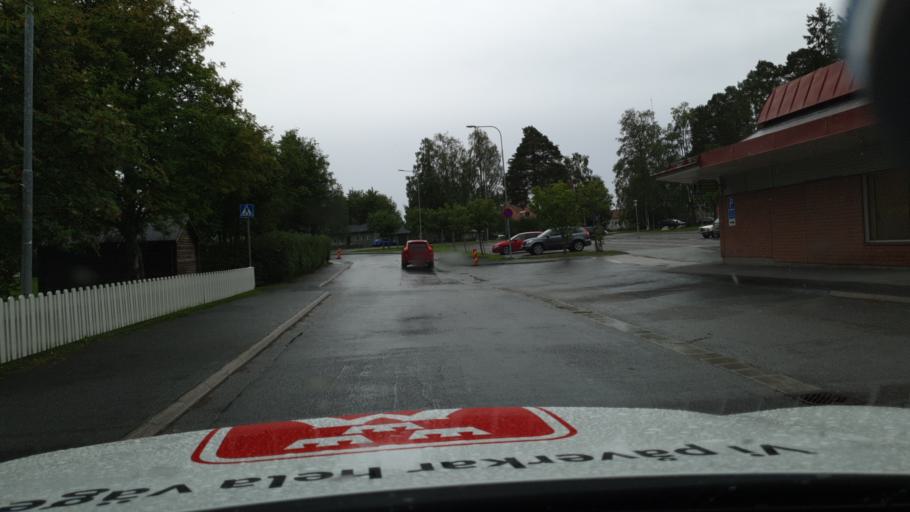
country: SE
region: Jaemtland
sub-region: Krokoms Kommun
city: Krokom
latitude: 63.3268
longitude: 14.4518
